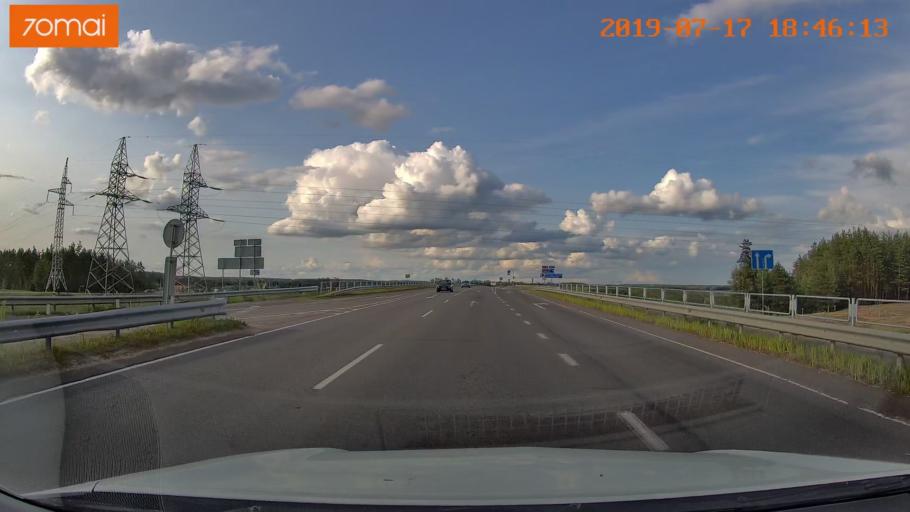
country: BY
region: Mogilev
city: Asipovichy
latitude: 53.3337
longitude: 28.6634
